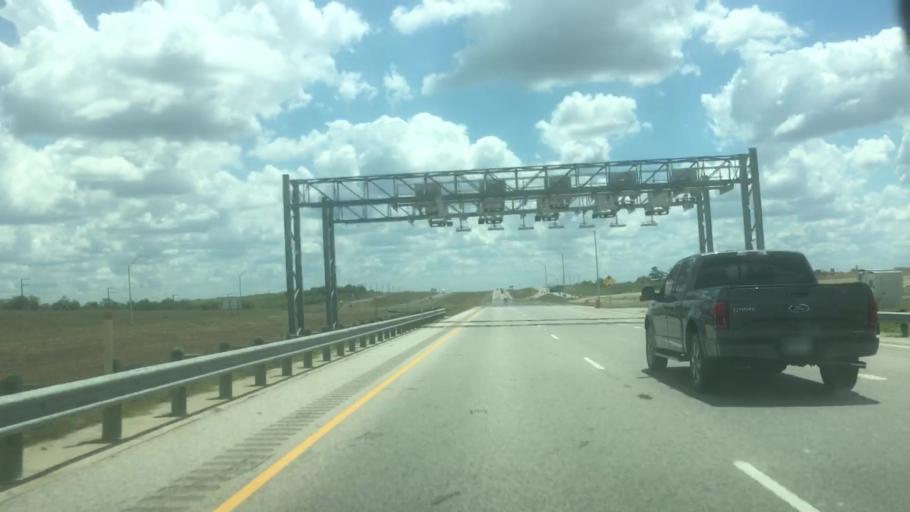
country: US
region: Texas
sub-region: Caldwell County
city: Lockhart
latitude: 29.9900
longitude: -97.6841
